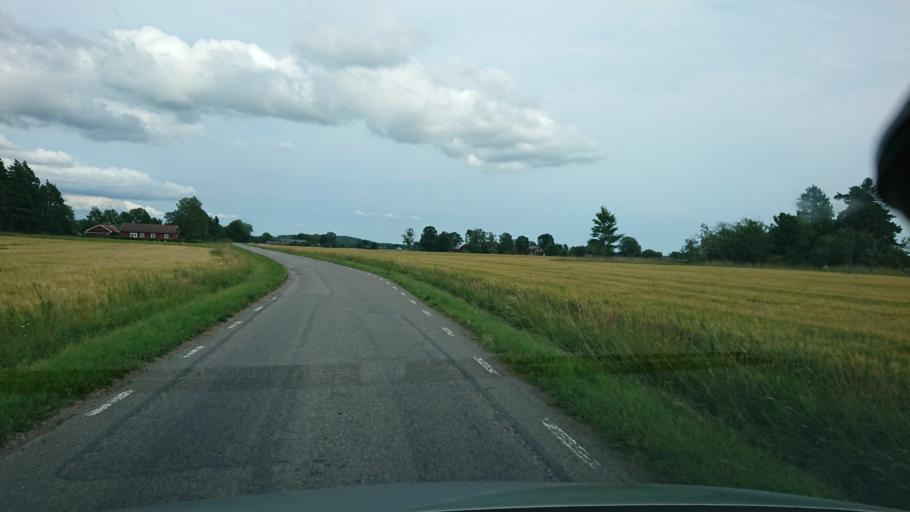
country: SE
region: Uppsala
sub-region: Osthammars Kommun
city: Bjorklinge
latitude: 59.9902
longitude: 17.5234
